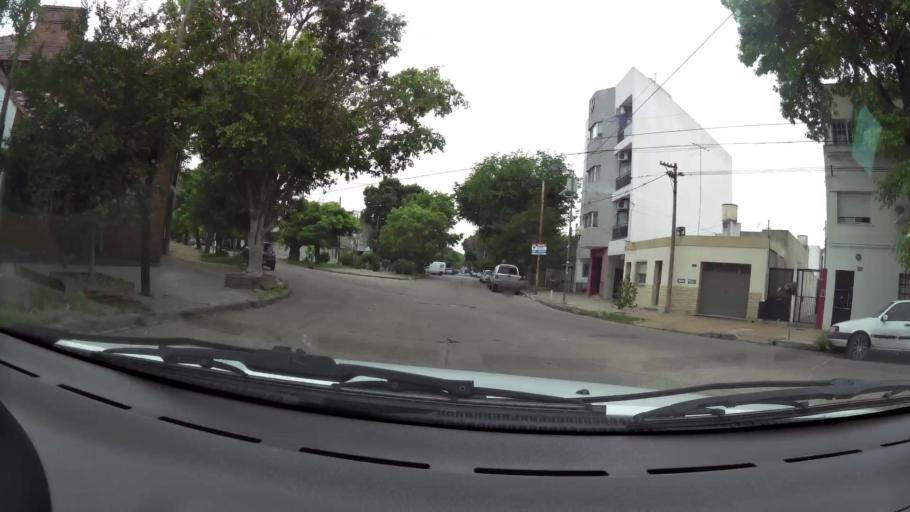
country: AR
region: Buenos Aires
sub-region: Partido de La Plata
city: La Plata
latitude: -34.9327
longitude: -57.9586
